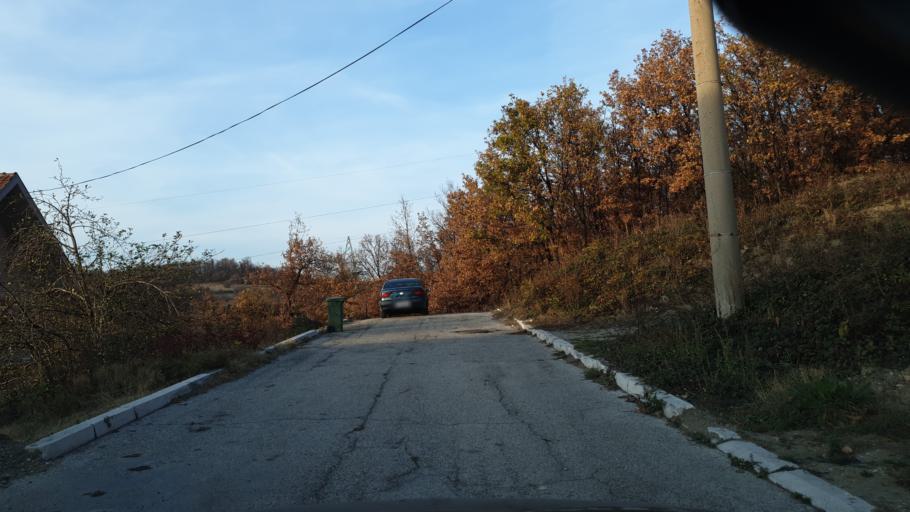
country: RS
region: Central Serbia
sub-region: Borski Okrug
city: Bor
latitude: 44.0600
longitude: 22.0798
